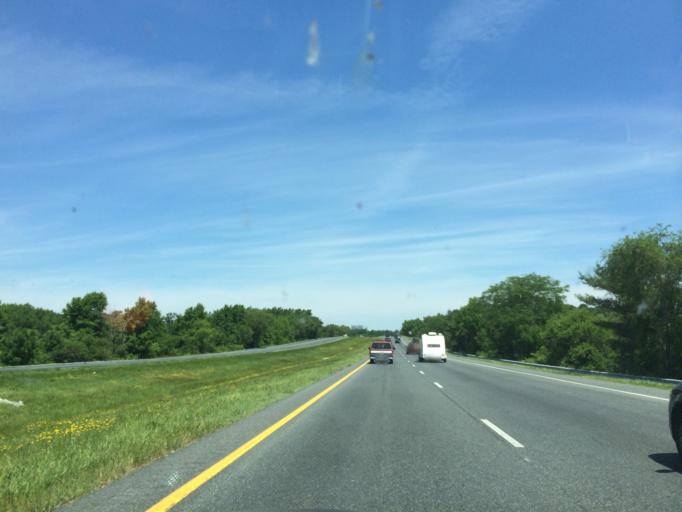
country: US
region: Maryland
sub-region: Wicomico County
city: Salisbury
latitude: 38.3761
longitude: -75.5389
